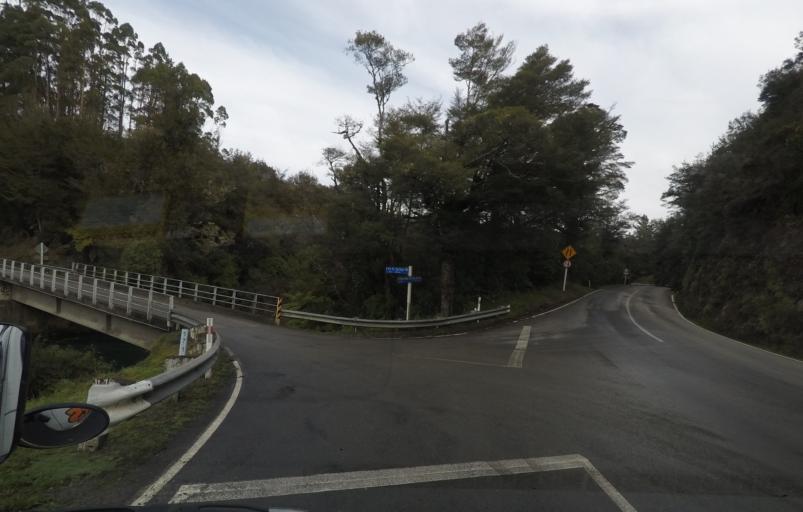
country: NZ
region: Tasman
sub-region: Tasman District
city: Takaka
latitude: -40.8413
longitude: 172.7772
